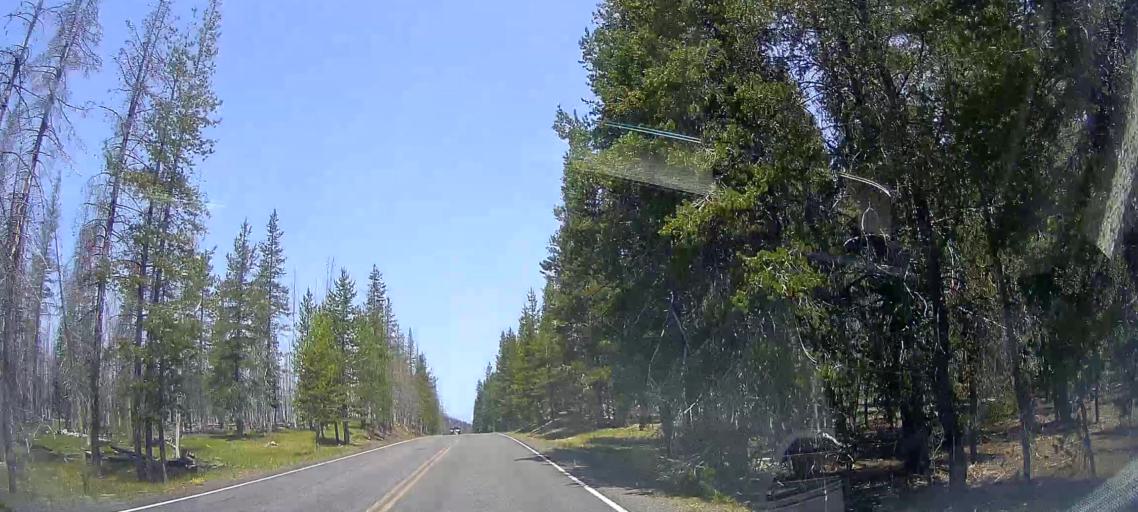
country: US
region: Oregon
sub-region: Lane County
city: Oakridge
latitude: 43.0488
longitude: -122.1202
